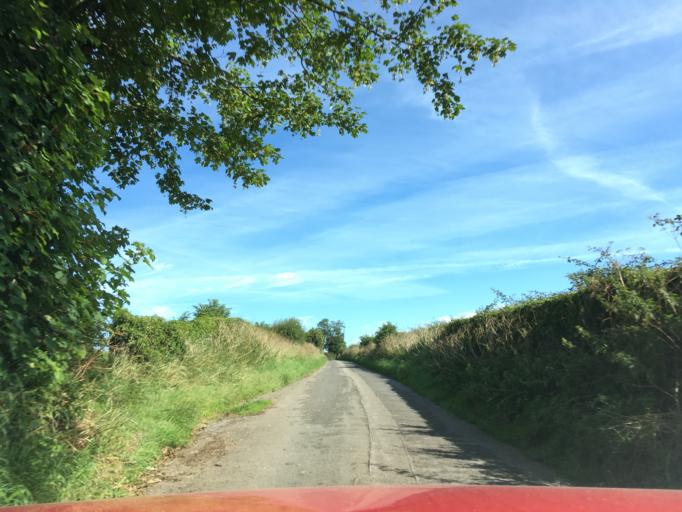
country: GB
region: England
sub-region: Wiltshire
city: Nettleton
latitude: 51.4746
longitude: -2.2641
